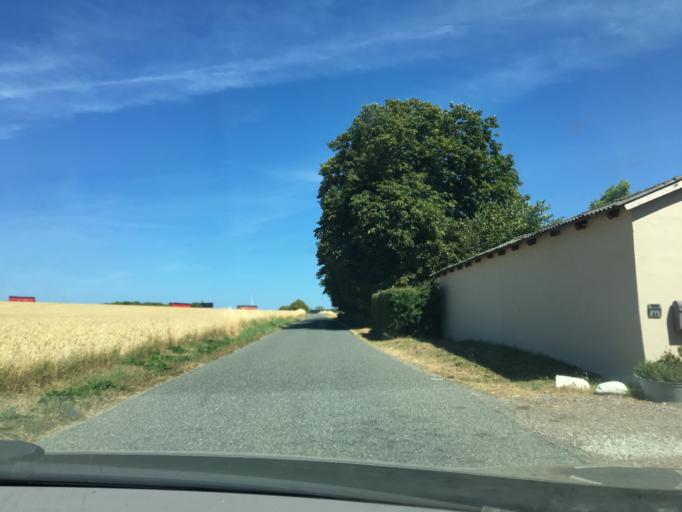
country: DK
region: South Denmark
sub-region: Middelfart Kommune
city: Norre Aby
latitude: 55.5159
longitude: 9.8387
